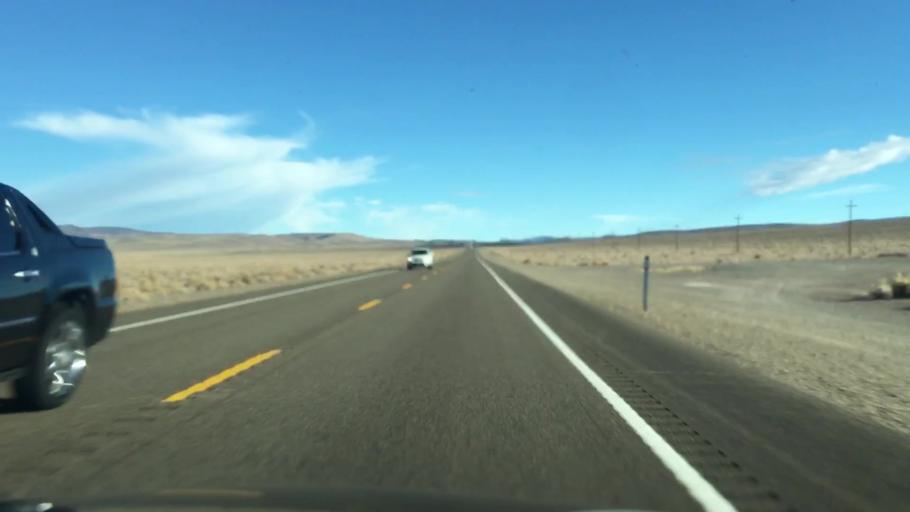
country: US
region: Nevada
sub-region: Mineral County
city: Hawthorne
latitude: 38.2536
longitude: -118.0800
